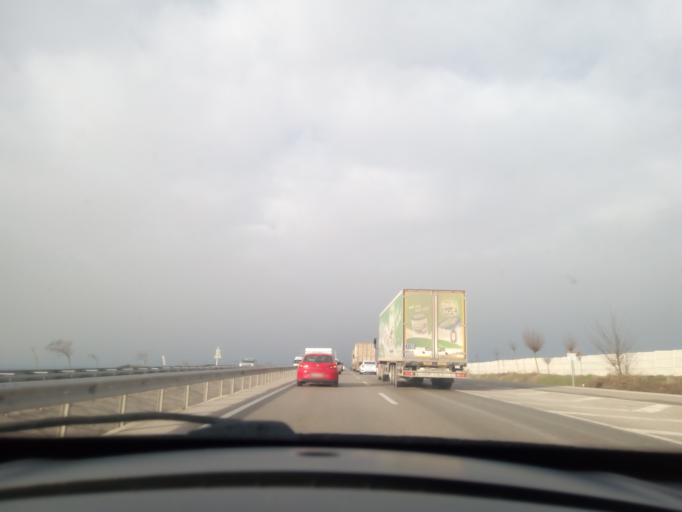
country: TR
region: Bursa
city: Mahmudiye
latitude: 40.2128
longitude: 28.6820
